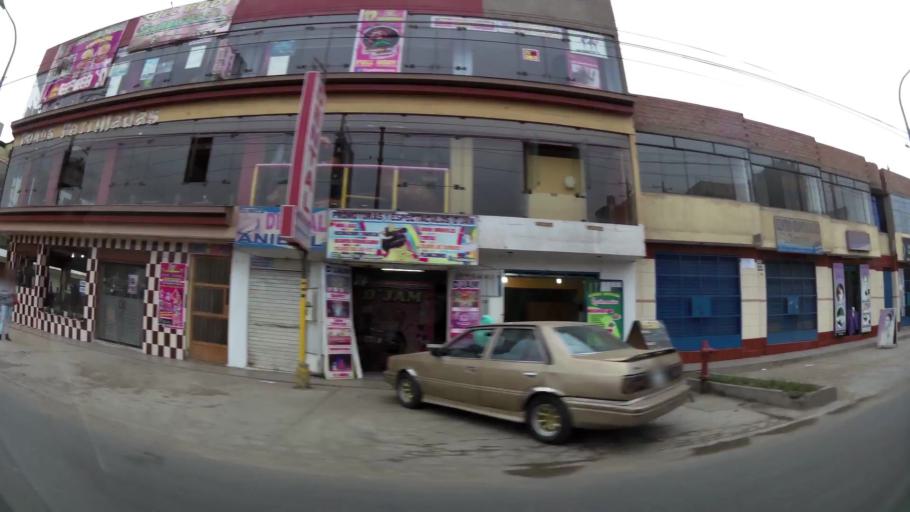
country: PE
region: Lima
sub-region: Lima
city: Urb. Santo Domingo
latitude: -11.8845
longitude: -77.0345
